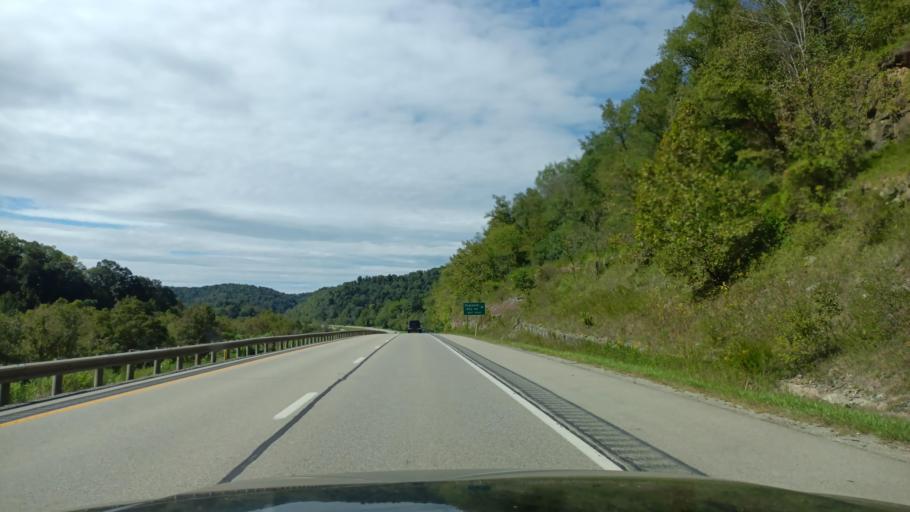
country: US
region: West Virginia
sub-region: Doddridge County
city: West Union
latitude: 39.2867
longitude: -80.7102
